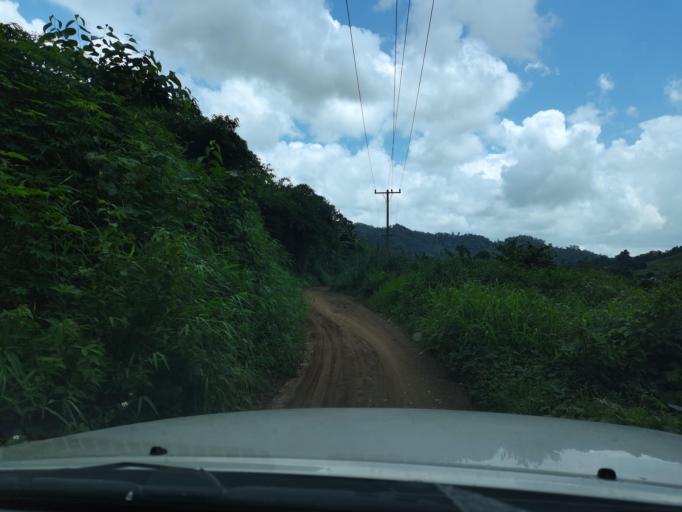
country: LA
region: Loungnamtha
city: Muang Long
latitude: 20.7560
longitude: 101.0171
